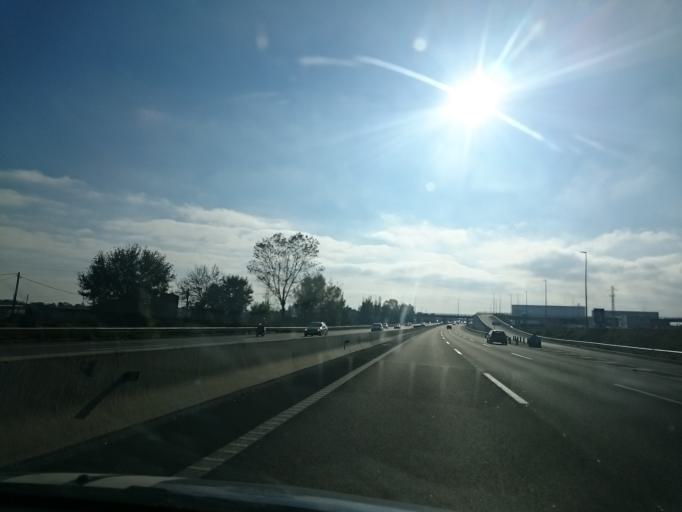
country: ES
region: Catalonia
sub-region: Provincia de Barcelona
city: Viladecans
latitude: 41.3062
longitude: 2.0273
